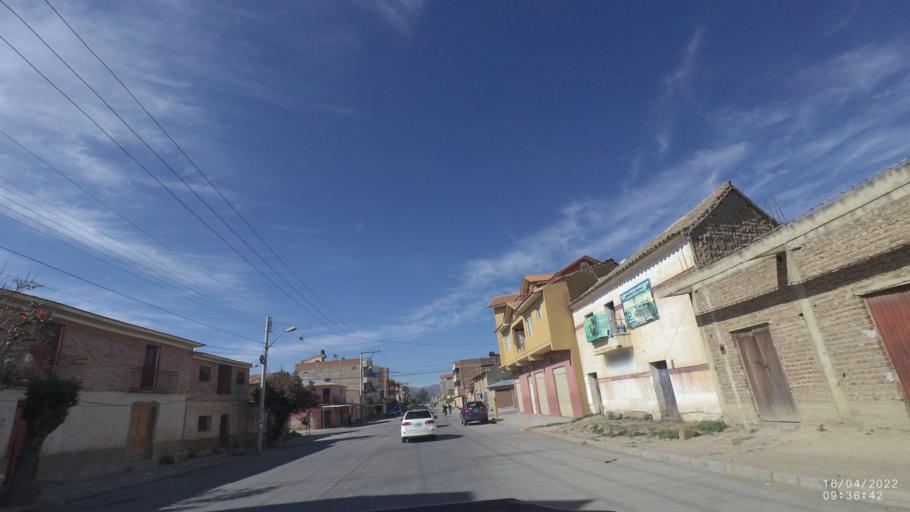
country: BO
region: Cochabamba
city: Punata
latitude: -17.5461
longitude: -65.8411
